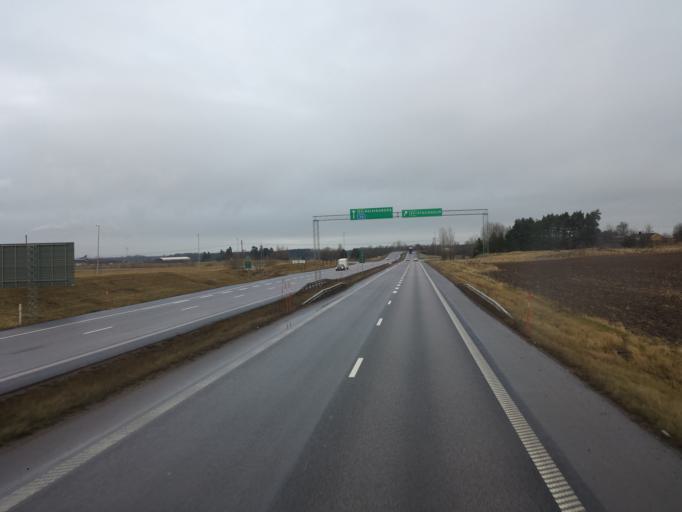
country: SE
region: OEstergoetland
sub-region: Linkopings Kommun
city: Linkoping
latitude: 58.4271
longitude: 15.6688
